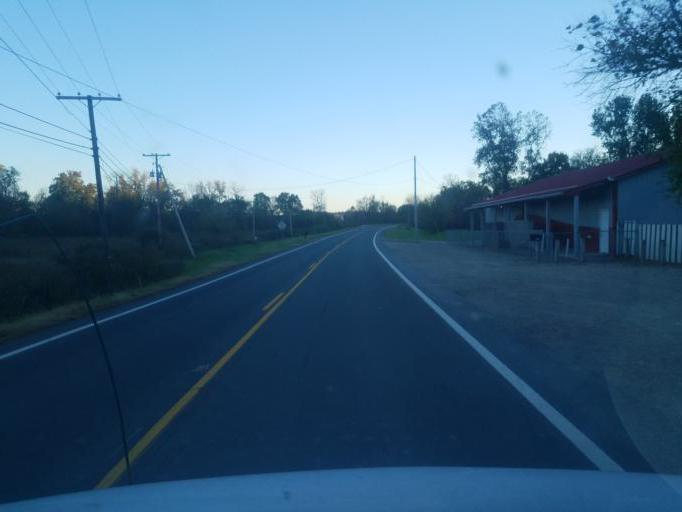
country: US
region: Ohio
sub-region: Licking County
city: Utica
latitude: 40.1814
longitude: -82.4212
